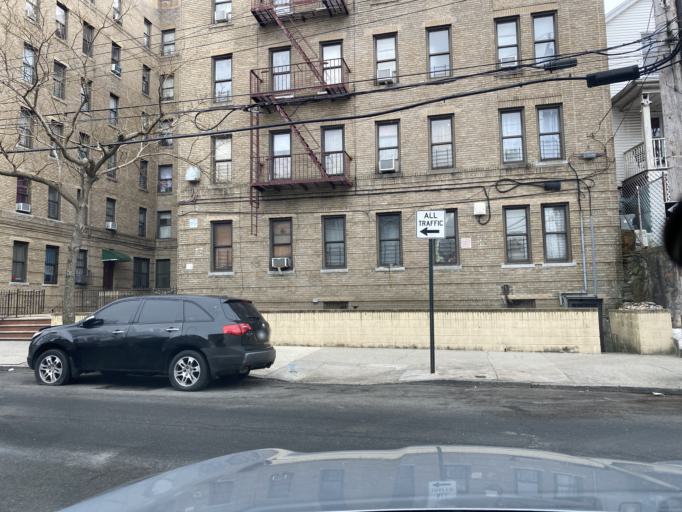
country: US
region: New York
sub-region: New York County
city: Inwood
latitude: 40.8776
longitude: -73.9003
